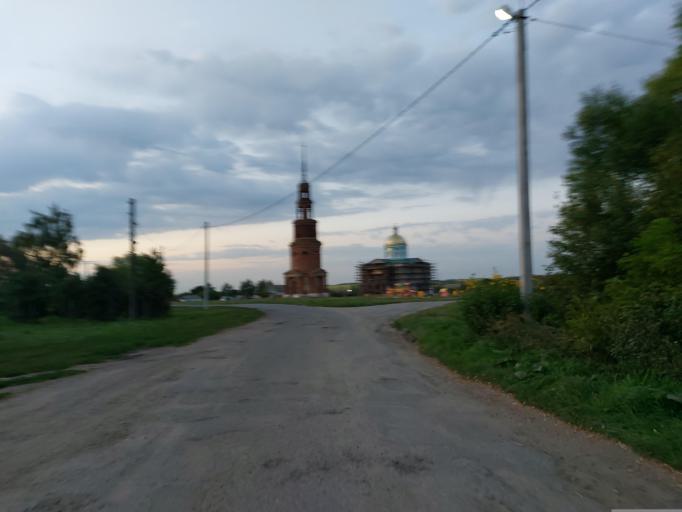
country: RU
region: Lipetsk
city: Dolgorukovo
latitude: 52.3761
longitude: 38.0514
